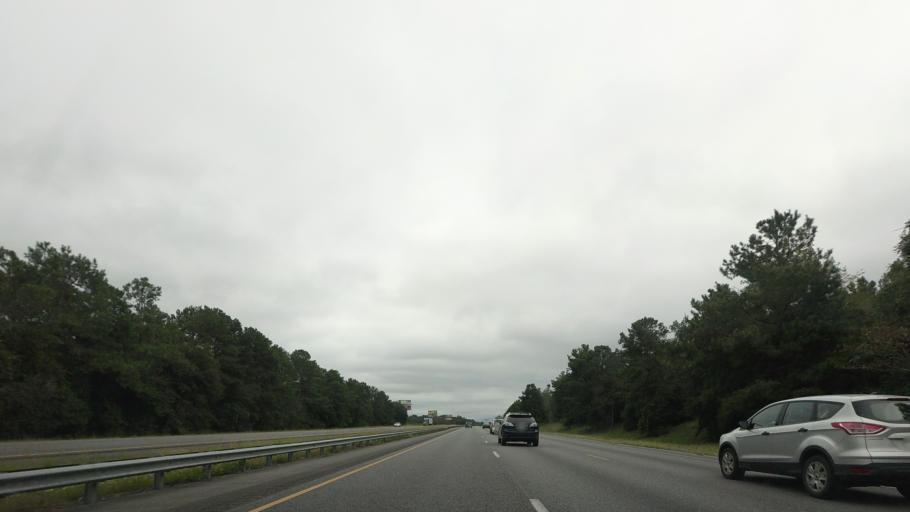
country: US
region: Georgia
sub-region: Lowndes County
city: Remerton
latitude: 30.8038
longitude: -83.3085
